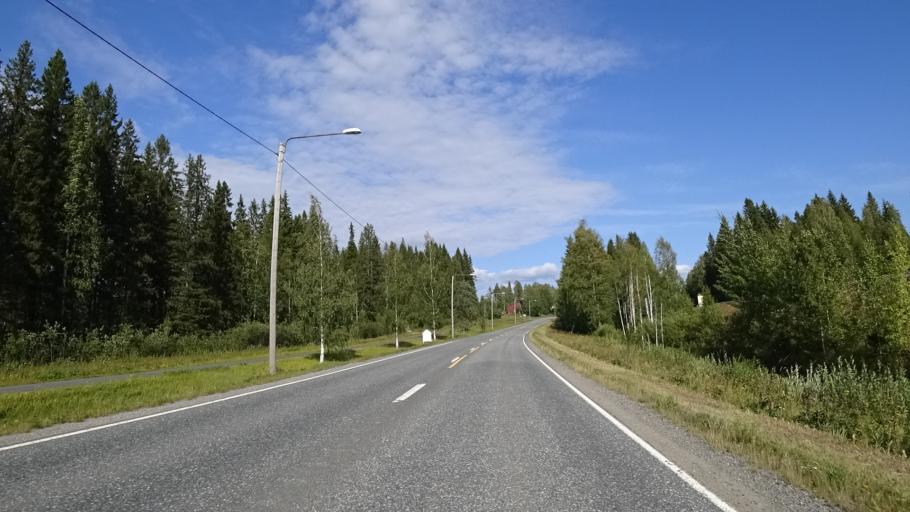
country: FI
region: North Karelia
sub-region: Joensuu
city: Eno
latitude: 62.8043
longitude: 30.1252
